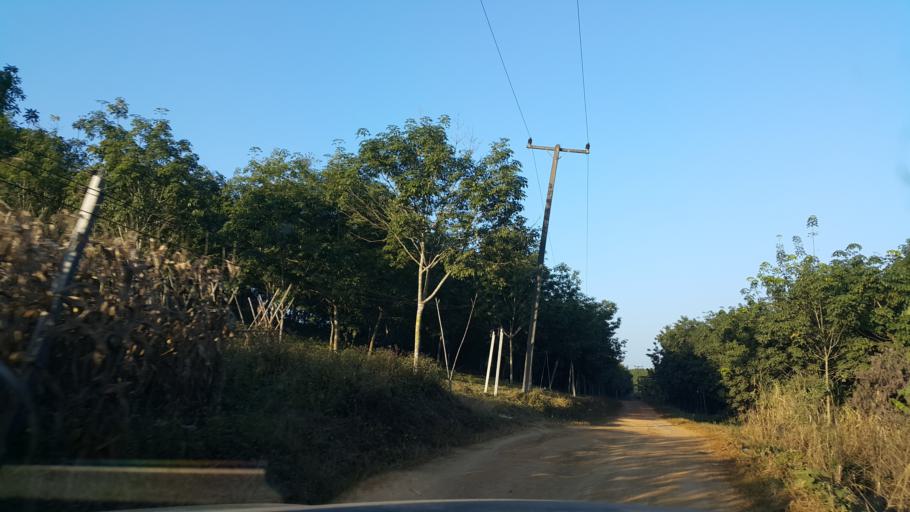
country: TH
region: Sukhothai
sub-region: Amphoe Si Satchanalai
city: Si Satchanalai
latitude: 17.6041
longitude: 99.6145
